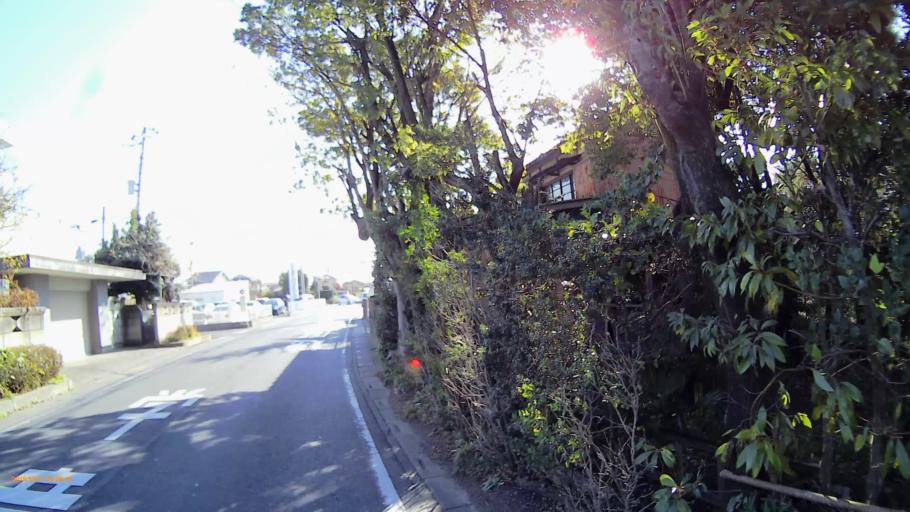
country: JP
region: Saitama
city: Menuma
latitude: 36.1757
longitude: 139.3430
